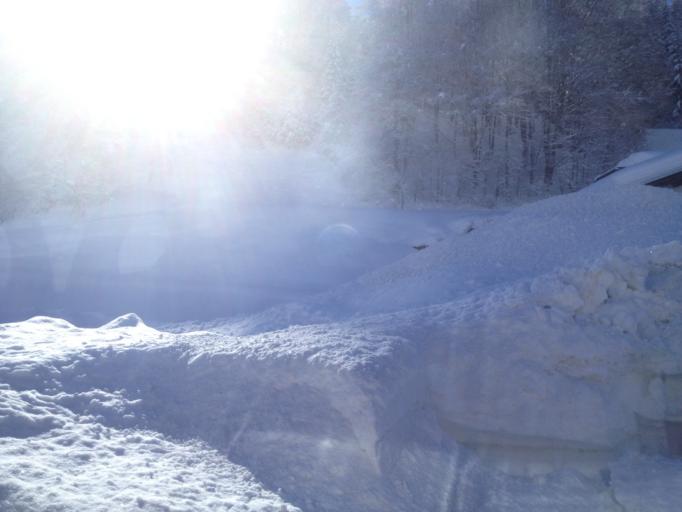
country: CH
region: Grisons
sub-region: Praettigau/Davos District
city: Klosters Serneus
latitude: 46.8610
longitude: 9.8986
